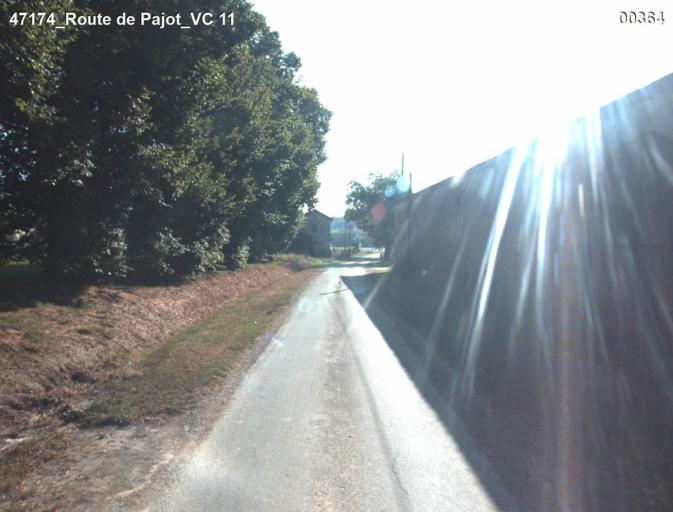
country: FR
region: Aquitaine
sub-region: Departement du Lot-et-Garonne
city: Nerac
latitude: 44.0824
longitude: 0.3623
